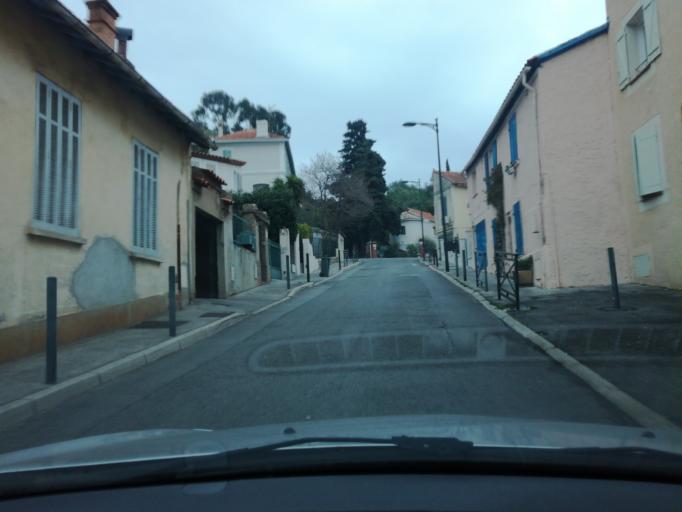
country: FR
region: Provence-Alpes-Cote d'Azur
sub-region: Departement du Var
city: Hyeres
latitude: 43.1223
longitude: 6.1208
